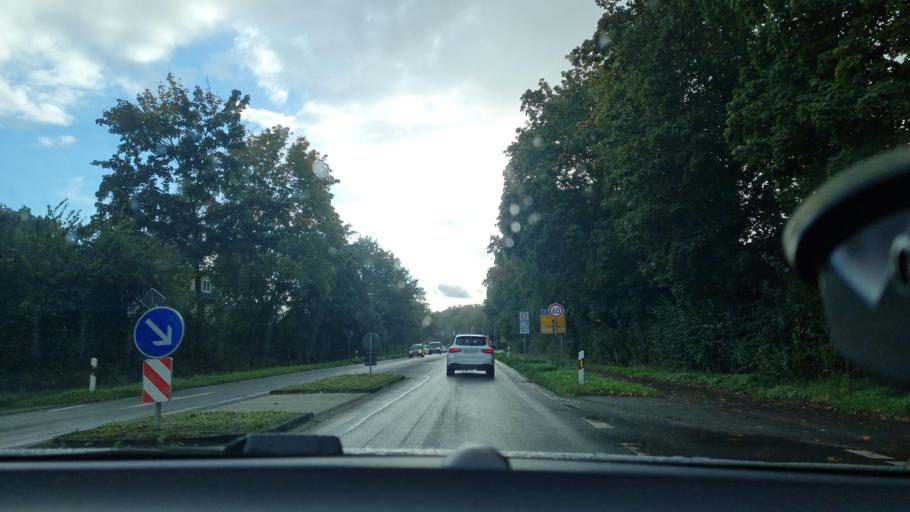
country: DE
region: North Rhine-Westphalia
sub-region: Regierungsbezirk Dusseldorf
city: Dinslaken
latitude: 51.5665
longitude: 6.7279
